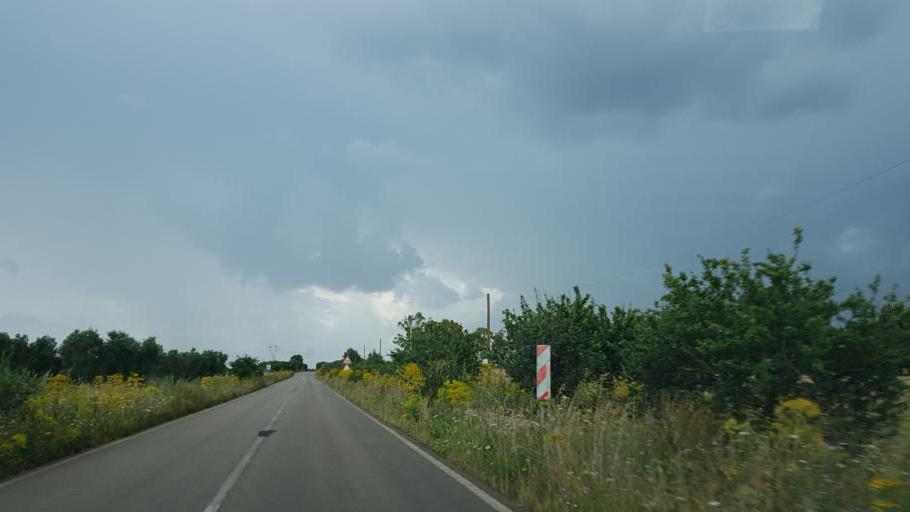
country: IT
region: Apulia
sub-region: Provincia di Brindisi
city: San Pancrazio Salentino
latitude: 40.3356
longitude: 17.8506
